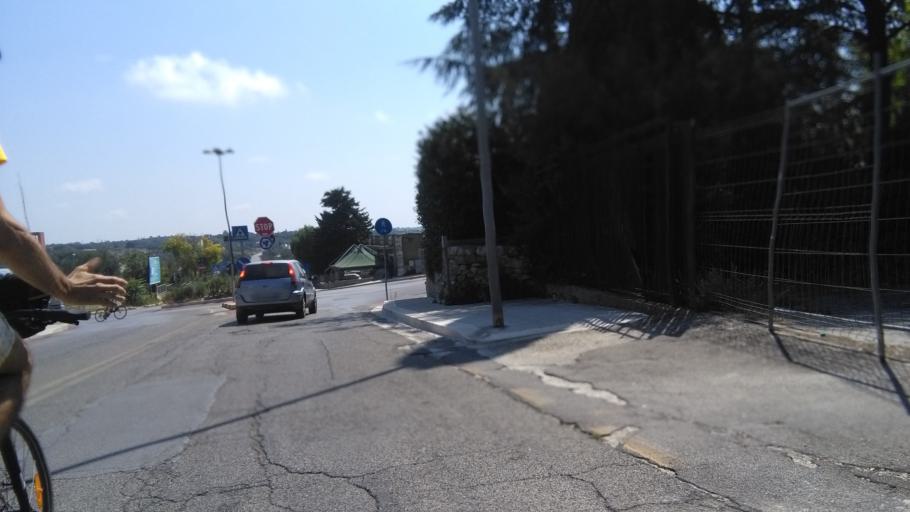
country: IT
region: Apulia
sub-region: Provincia di Bari
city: Putignano
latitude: 40.8467
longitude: 17.1277
